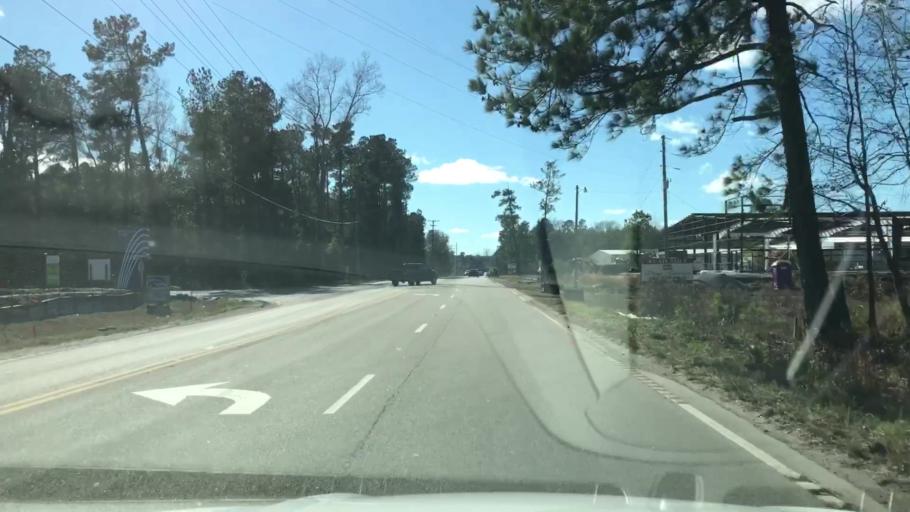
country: US
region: South Carolina
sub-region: Dorchester County
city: Summerville
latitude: 33.0599
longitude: -80.2319
